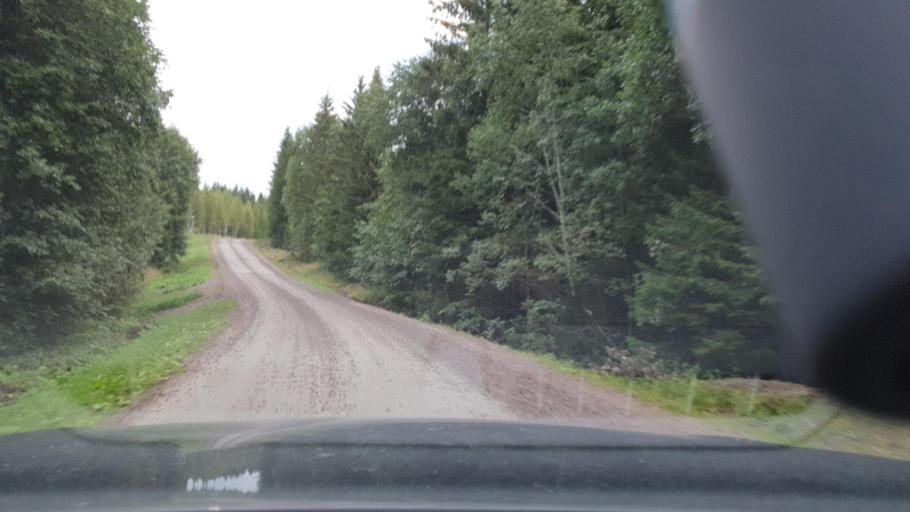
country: SE
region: Vaermland
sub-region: Munkfors Kommun
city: Munkfors
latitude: 59.8939
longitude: 13.4973
